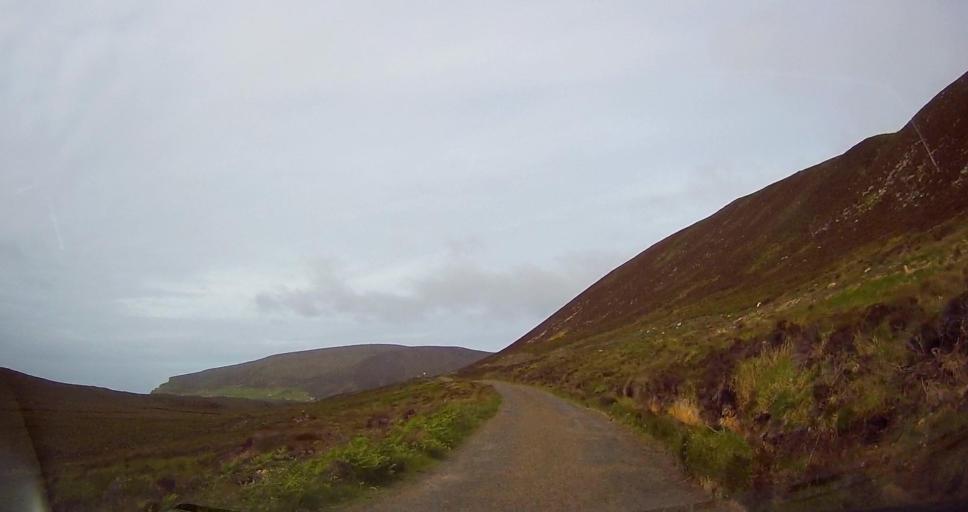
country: GB
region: Scotland
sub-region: Orkney Islands
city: Stromness
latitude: 58.8821
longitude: -3.3545
